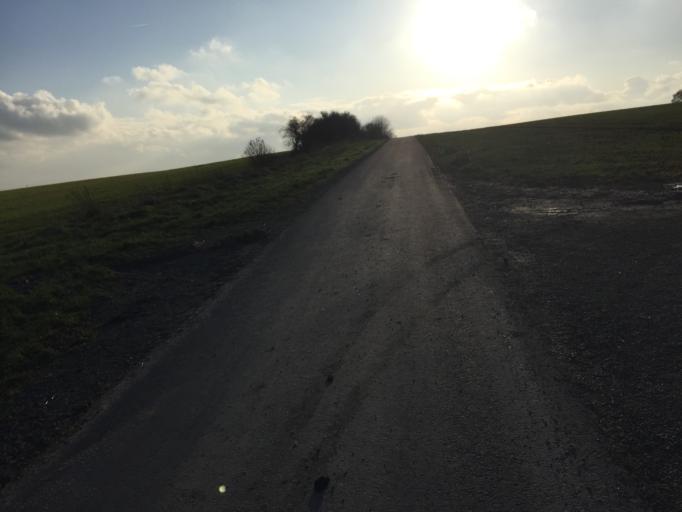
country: DE
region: Hesse
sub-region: Regierungsbezirk Giessen
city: Langgons
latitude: 50.5151
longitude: 8.7116
